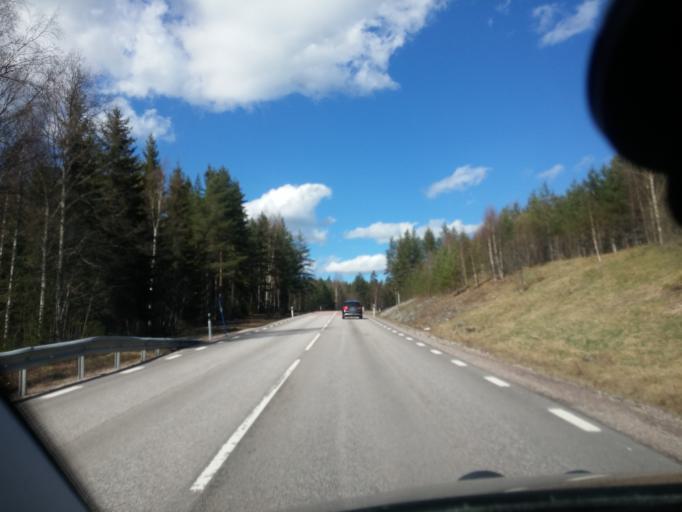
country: SE
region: Dalarna
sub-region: Faluns Kommun
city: Svardsjo
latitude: 60.7294
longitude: 15.7660
